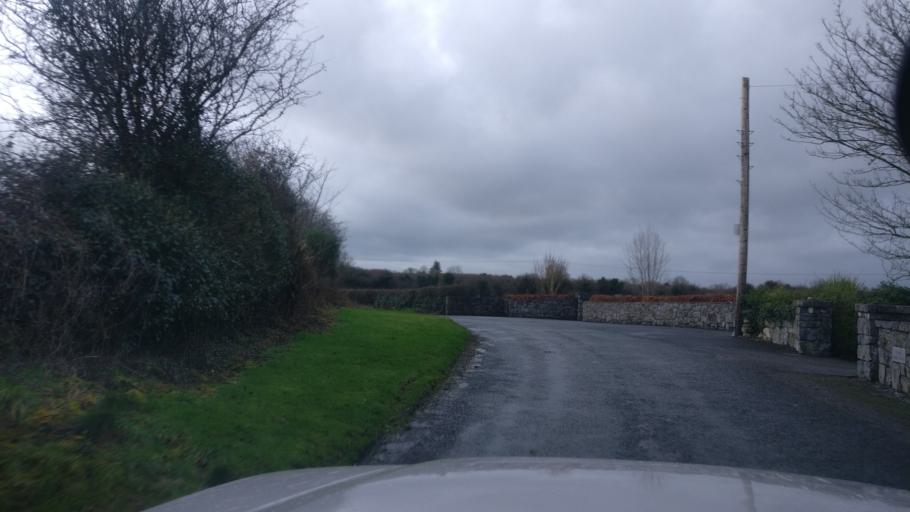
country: IE
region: Connaught
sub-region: County Galway
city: Athenry
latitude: 53.2615
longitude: -8.7994
